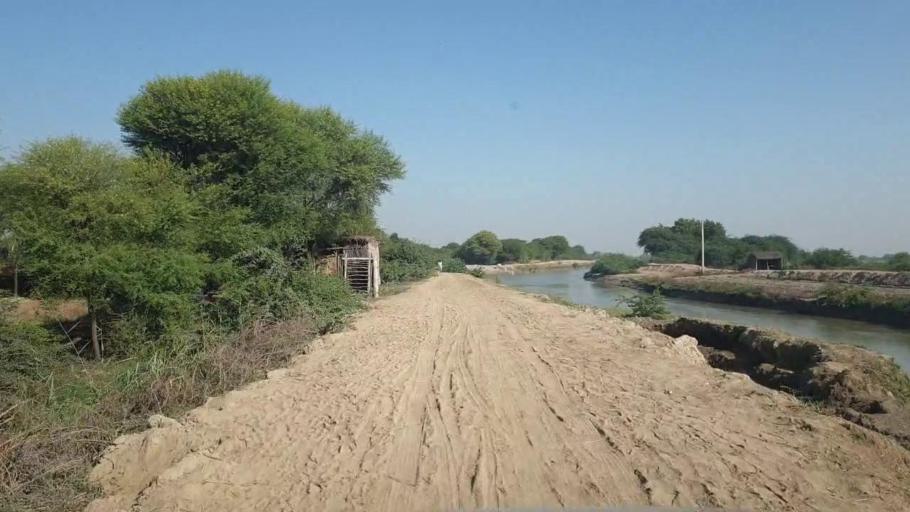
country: PK
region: Sindh
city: Badin
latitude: 24.7226
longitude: 68.8030
